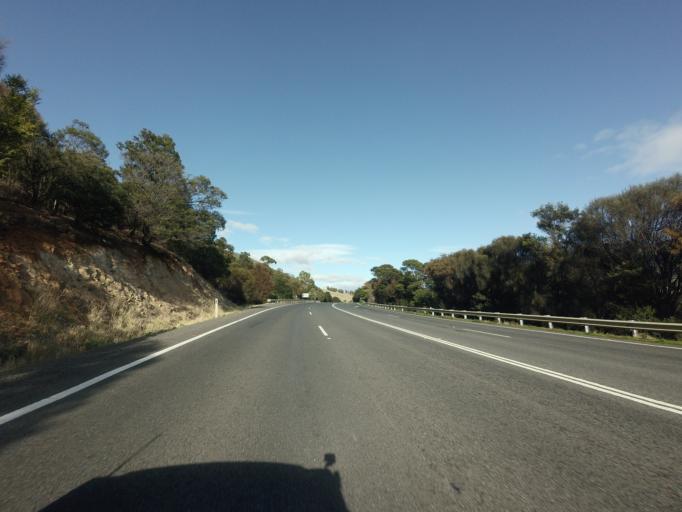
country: AU
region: Tasmania
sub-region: Glenorchy
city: Granton
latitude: -42.7514
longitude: 147.1724
